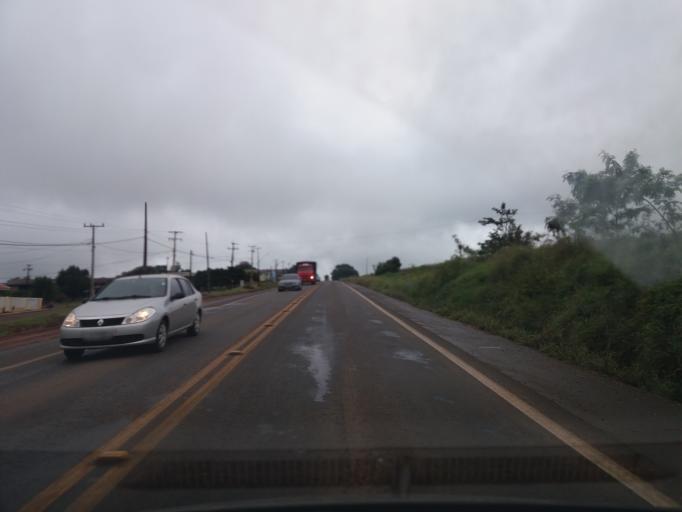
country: BR
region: Parana
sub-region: Cascavel
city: Cascavel
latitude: -25.2742
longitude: -53.5690
